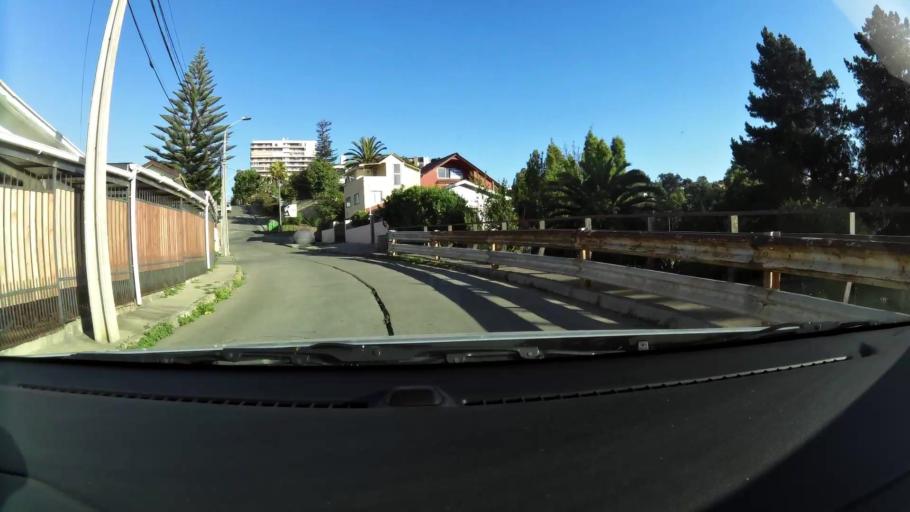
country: CL
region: Valparaiso
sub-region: Provincia de Valparaiso
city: Vina del Mar
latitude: -33.0310
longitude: -71.5836
